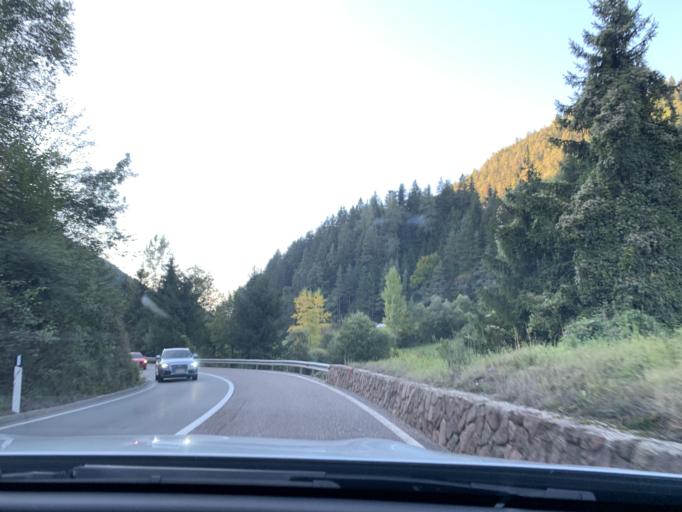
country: IT
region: Trentino-Alto Adige
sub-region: Bolzano
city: Nova Ponente
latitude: 46.4321
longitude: 11.4756
